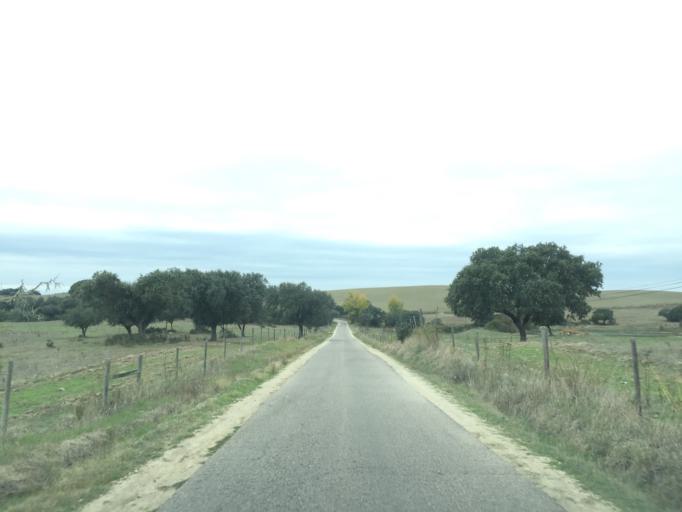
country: PT
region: Portalegre
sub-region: Fronteira
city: Vale da Amoreira
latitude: 39.0508
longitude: -7.7921
